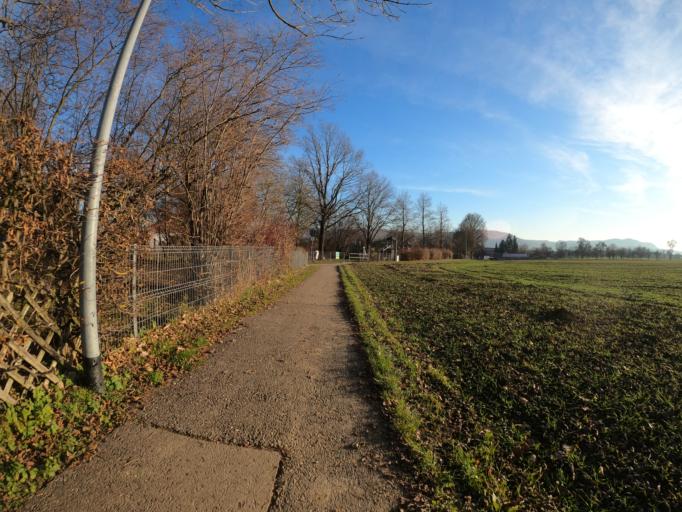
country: DE
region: Baden-Wuerttemberg
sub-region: Regierungsbezirk Stuttgart
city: Boll
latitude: 48.6689
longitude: 9.6123
